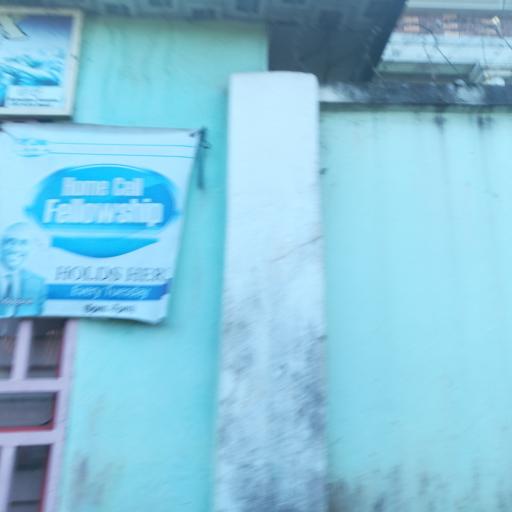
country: NG
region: Rivers
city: Port Harcourt
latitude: 4.8606
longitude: 6.9653
